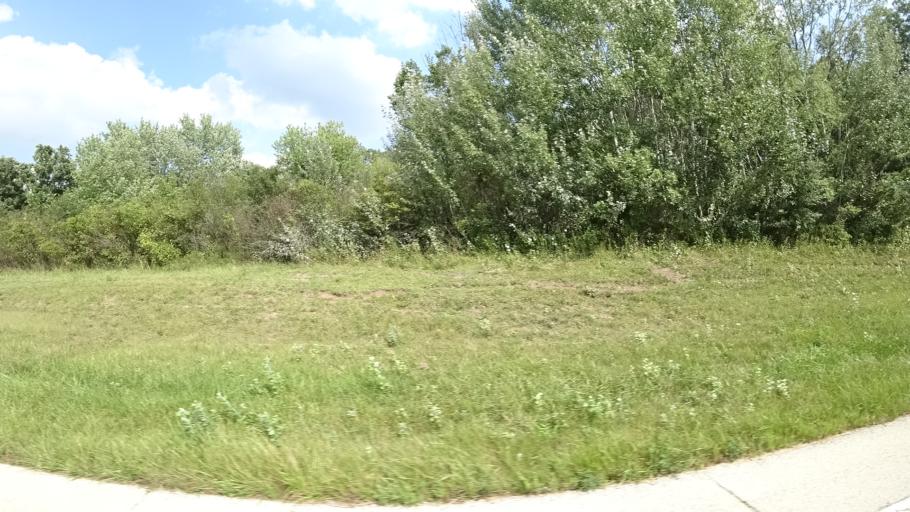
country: US
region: Illinois
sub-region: Will County
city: Goodings Grove
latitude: 41.6557
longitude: -87.9123
